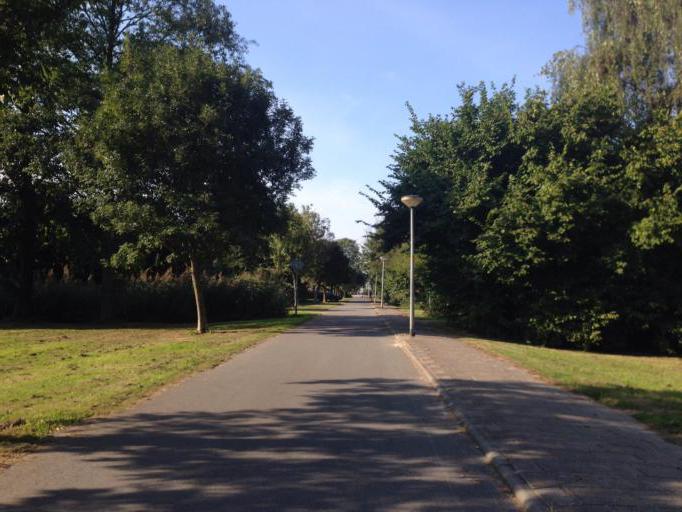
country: NL
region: Flevoland
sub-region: Gemeente Almere
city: Almere Stad
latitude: 52.3921
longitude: 5.2628
